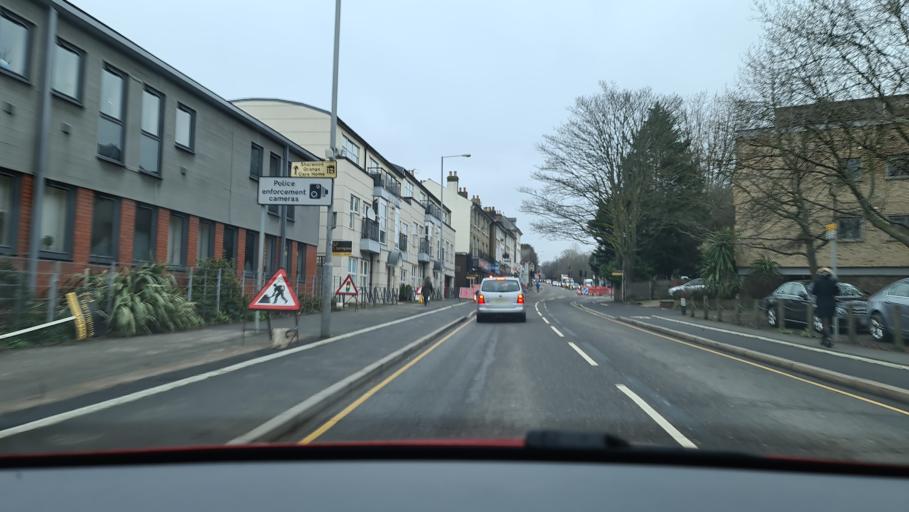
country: GB
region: England
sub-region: Greater London
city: Kingston upon Thames
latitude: 51.4152
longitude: -0.2856
